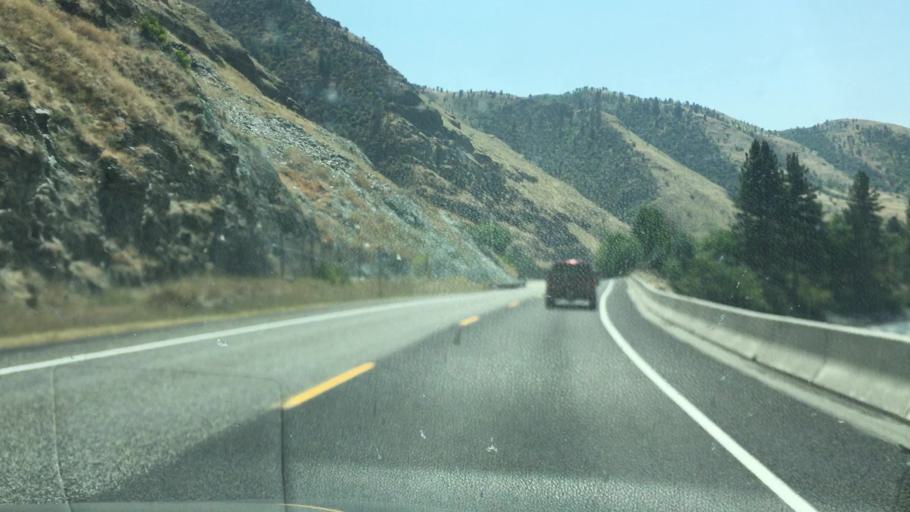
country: US
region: Idaho
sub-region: Idaho County
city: Grangeville
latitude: 45.6059
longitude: -116.2717
